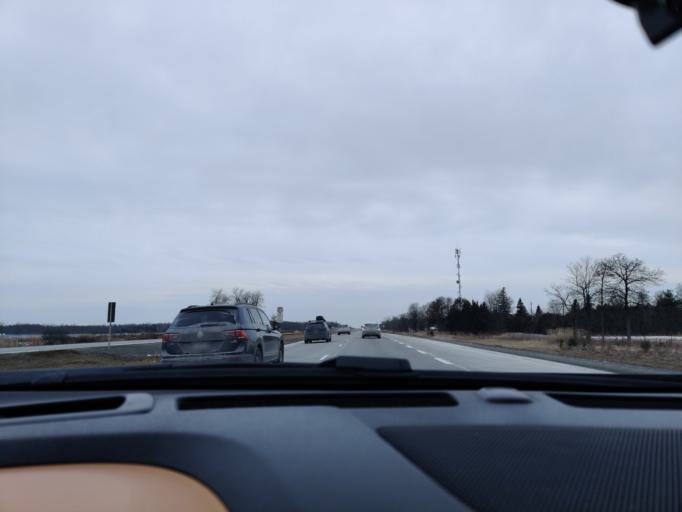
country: US
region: New York
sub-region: St. Lawrence County
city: Massena
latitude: 45.0099
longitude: -75.0011
